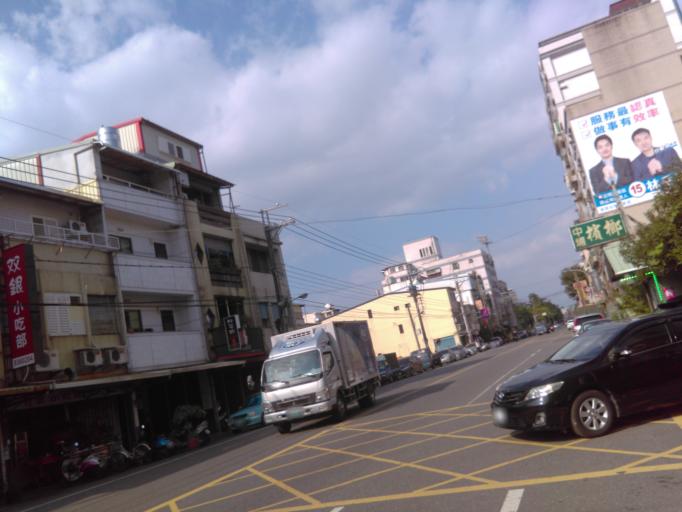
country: TW
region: Taiwan
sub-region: Yilan
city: Yilan
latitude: 24.7431
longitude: 121.7477
